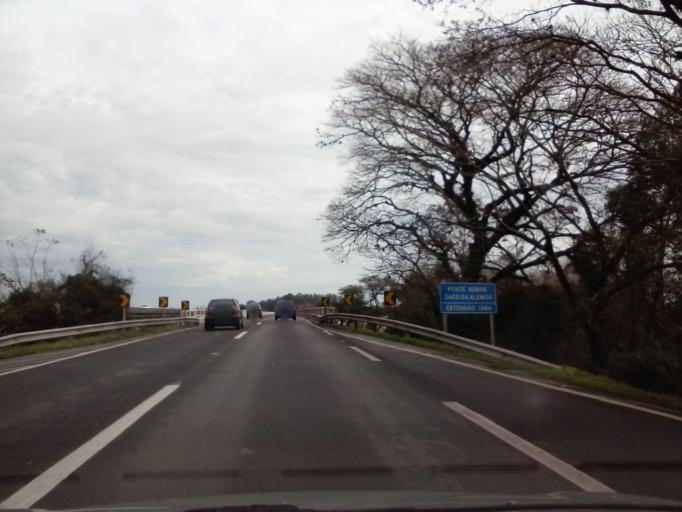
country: BR
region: Rio Grande do Sul
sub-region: Porto Alegre
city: Porto Alegre
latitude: -29.9896
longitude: -51.2326
